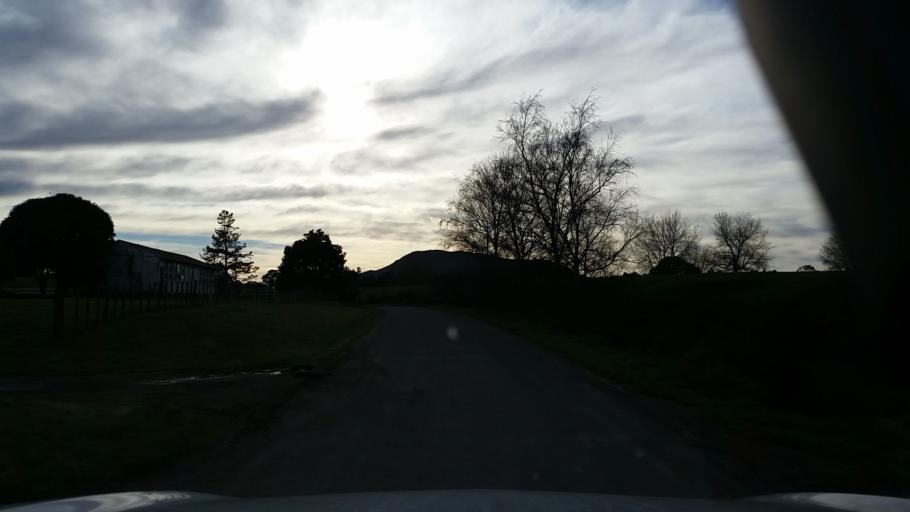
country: NZ
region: Bay of Plenty
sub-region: Rotorua District
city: Rotorua
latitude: -38.2658
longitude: 176.1577
